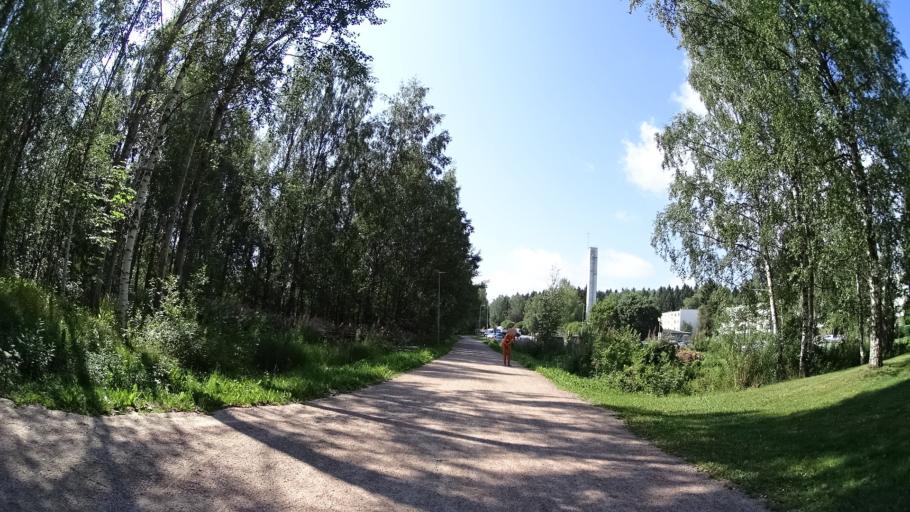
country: FI
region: Uusimaa
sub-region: Helsinki
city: Teekkarikylae
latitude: 60.2731
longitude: 24.8617
